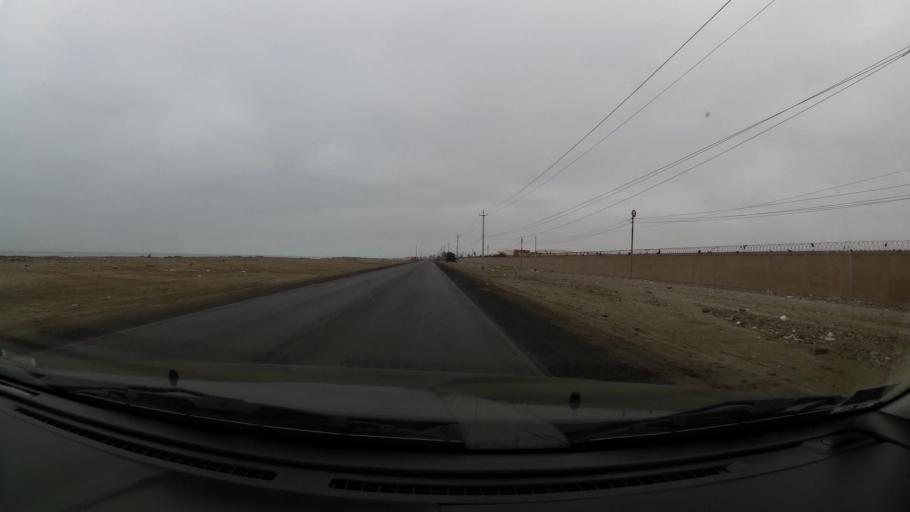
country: PE
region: Ica
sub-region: Provincia de Pisco
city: Pisco
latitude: -13.7510
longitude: -76.2297
